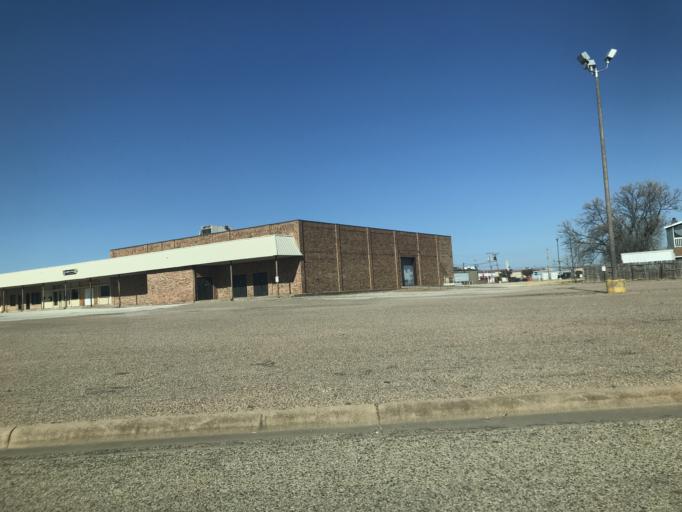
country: US
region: Texas
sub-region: Taylor County
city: Abilene
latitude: 32.4575
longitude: -99.7034
